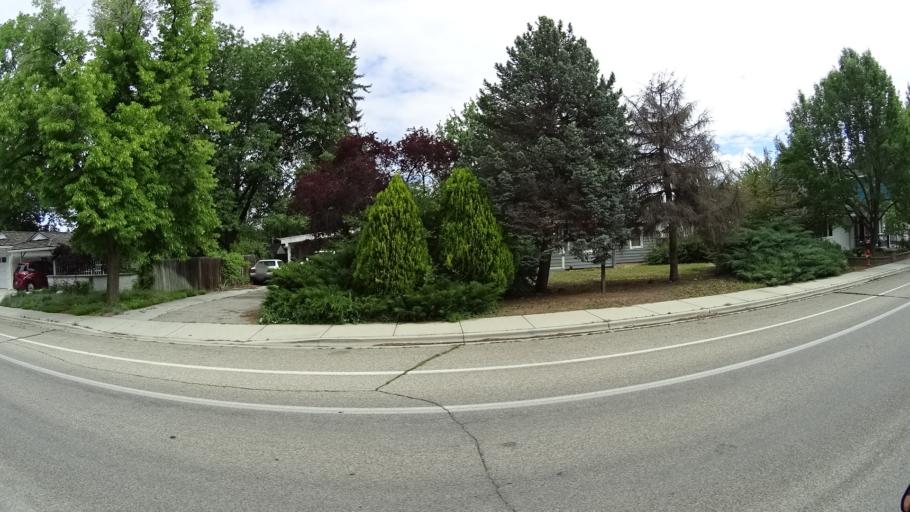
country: US
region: Idaho
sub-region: Ada County
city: Boise
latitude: 43.5789
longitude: -116.1880
